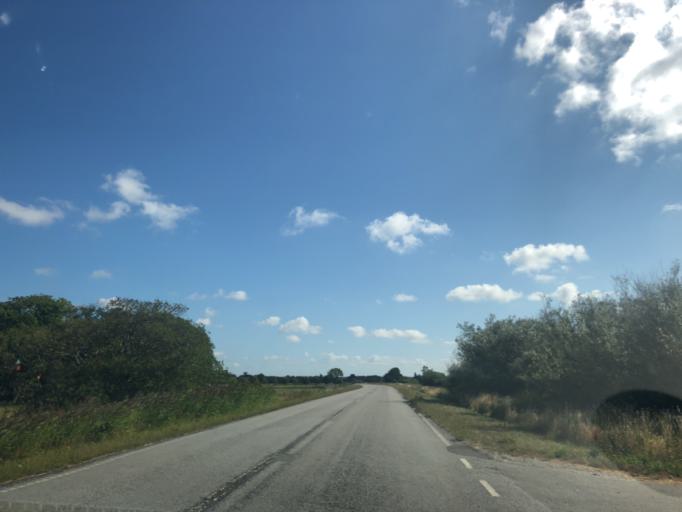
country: DK
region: North Denmark
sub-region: Morso Kommune
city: Nykobing Mors
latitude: 57.0179
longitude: 8.9838
